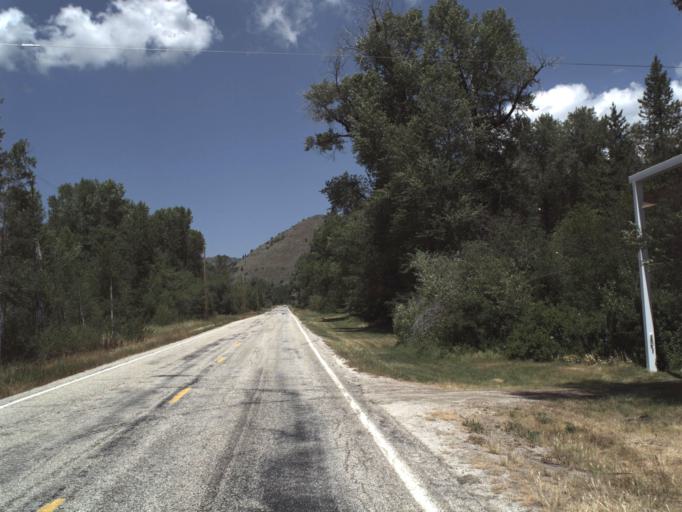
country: US
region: Utah
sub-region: Weber County
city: Wolf Creek
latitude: 41.3043
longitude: -111.6176
